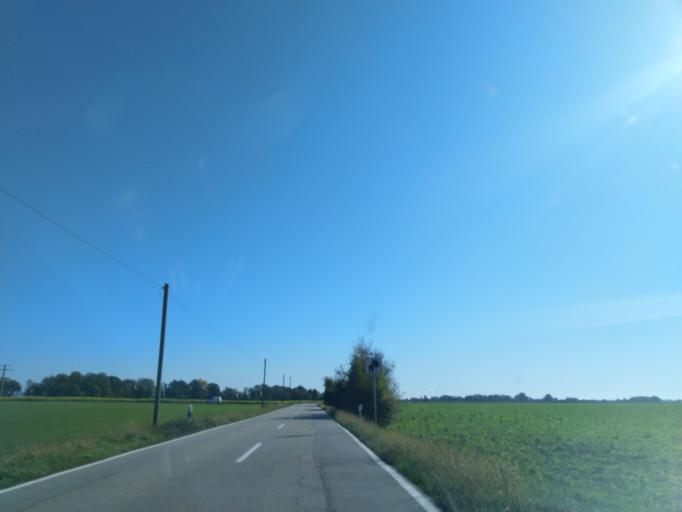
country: DE
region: Bavaria
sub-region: Lower Bavaria
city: Irlbach
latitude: 48.8387
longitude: 12.7594
